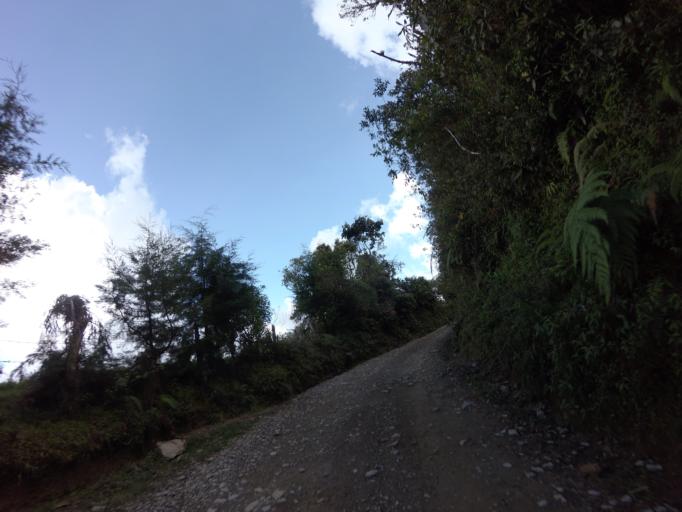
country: CO
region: Caldas
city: Pensilvania
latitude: 5.4431
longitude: -75.1290
